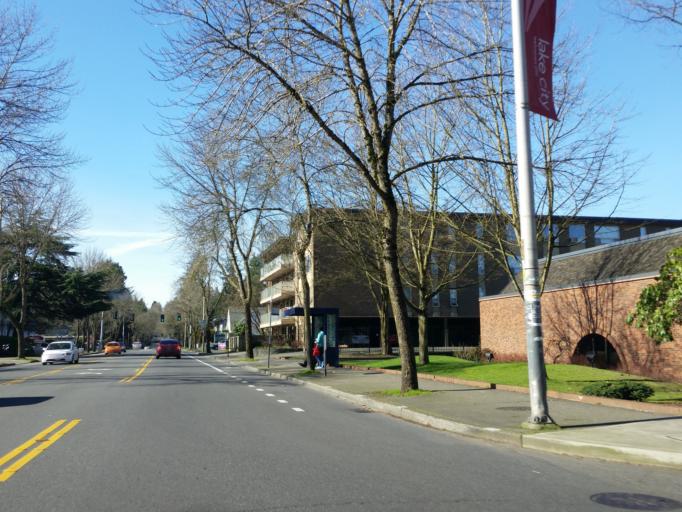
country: US
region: Washington
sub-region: King County
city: Lake Forest Park
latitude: 47.7194
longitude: -122.2978
